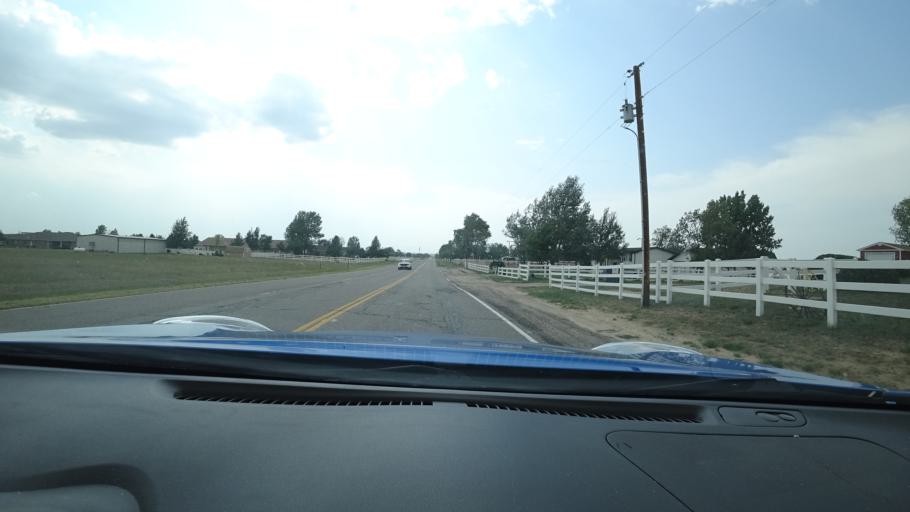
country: US
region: Colorado
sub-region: Adams County
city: Brighton
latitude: 39.9216
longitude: -104.8339
